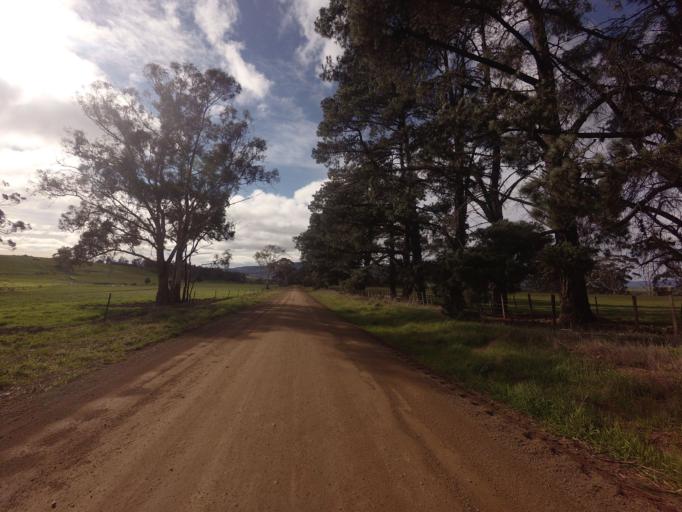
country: AU
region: Tasmania
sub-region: Derwent Valley
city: New Norfolk
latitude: -42.7156
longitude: 146.8829
